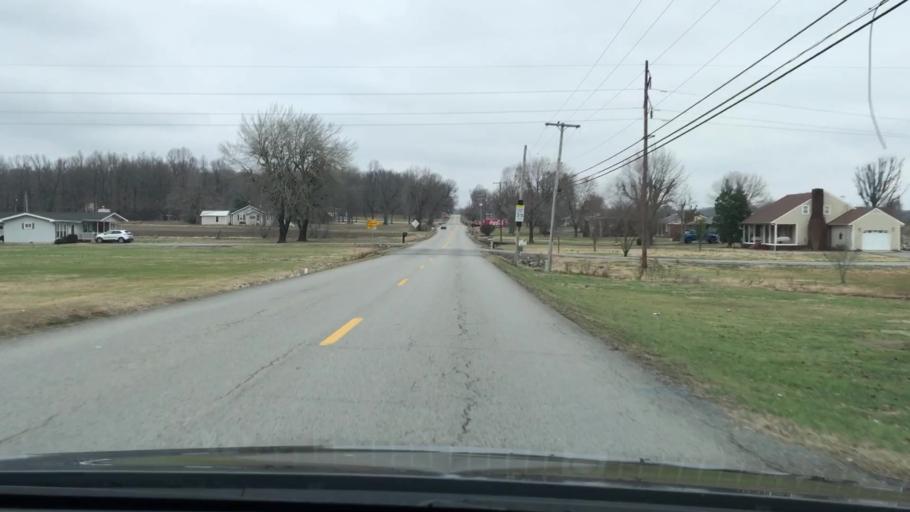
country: US
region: Kentucky
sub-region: Muhlenberg County
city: Greenville
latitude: 37.2212
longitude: -87.1938
